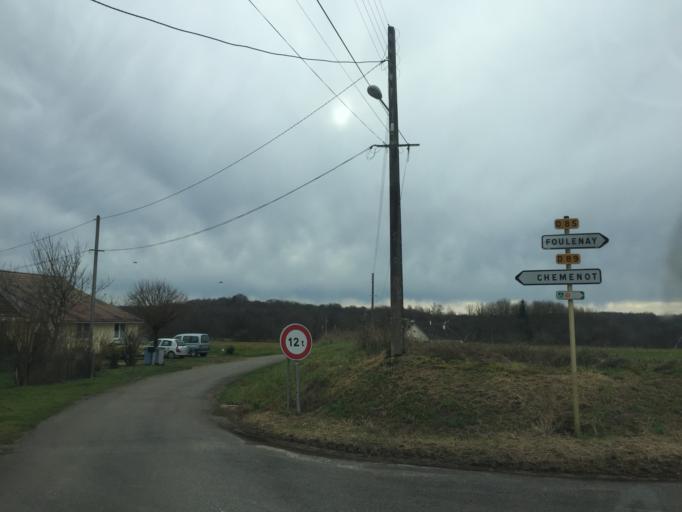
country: FR
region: Franche-Comte
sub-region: Departement du Jura
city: Mont-sous-Vaudrey
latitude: 46.8692
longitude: 5.5223
